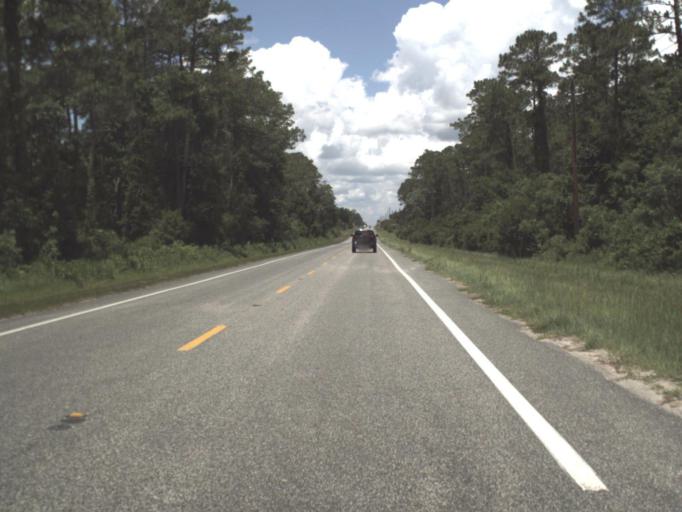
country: US
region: Florida
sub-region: Putnam County
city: Crescent City
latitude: 29.4813
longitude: -81.5533
